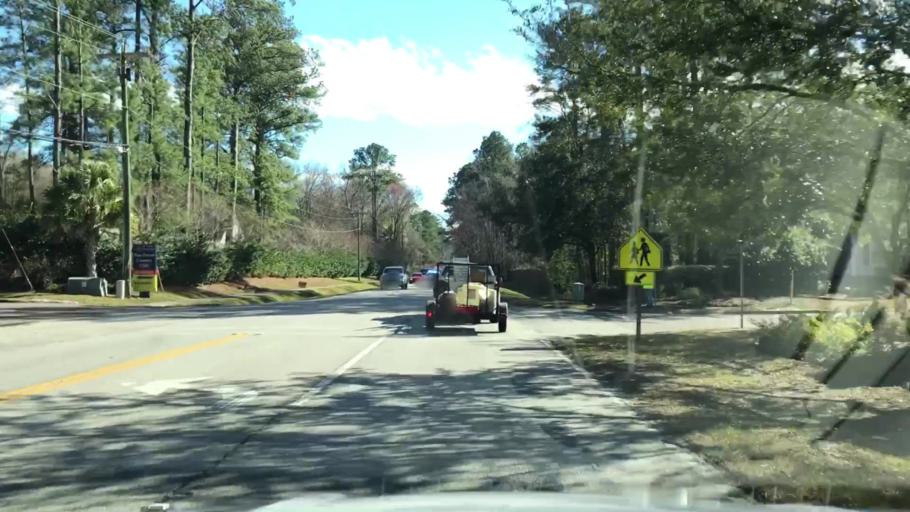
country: US
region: South Carolina
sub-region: Dorchester County
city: Summerville
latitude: 33.0299
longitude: -80.2448
